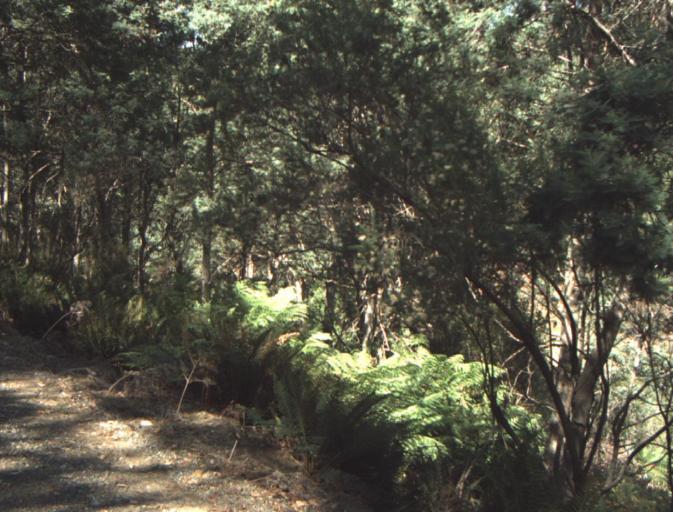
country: AU
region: Tasmania
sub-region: Dorset
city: Scottsdale
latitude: -41.2824
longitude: 147.3394
